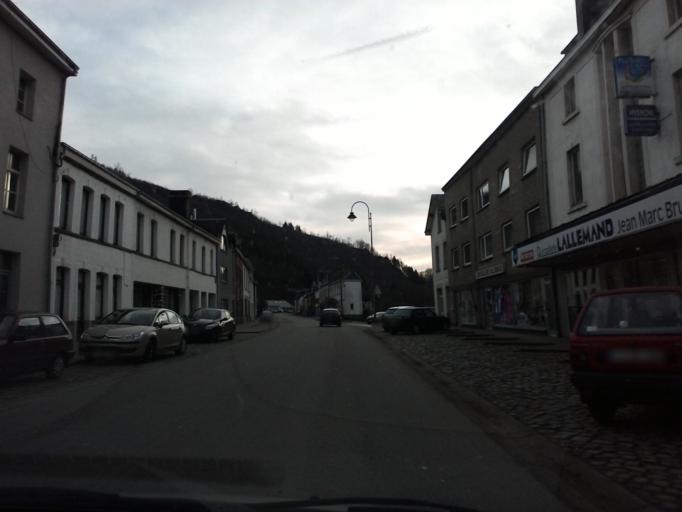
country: BE
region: Wallonia
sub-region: Province du Luxembourg
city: Vielsalm
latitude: 50.2787
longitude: 5.9110
